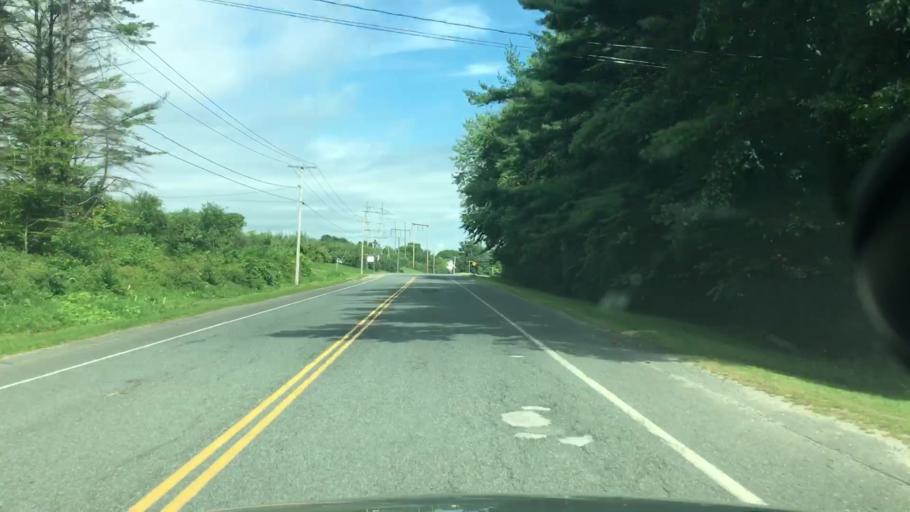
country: US
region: Massachusetts
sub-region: Franklin County
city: Colrain
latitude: 42.6512
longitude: -72.6763
